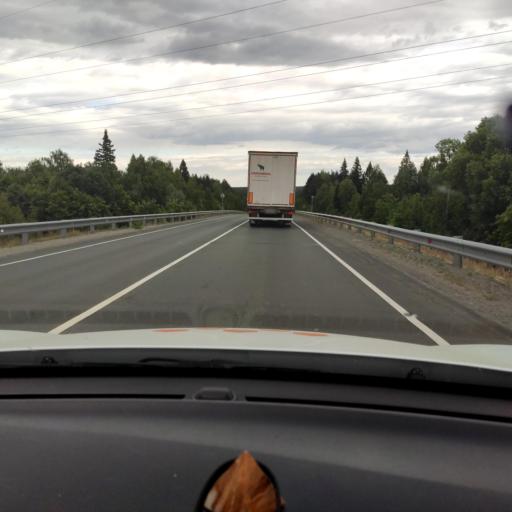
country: RU
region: Mariy-El
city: Volzhsk
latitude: 55.9079
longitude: 48.3745
